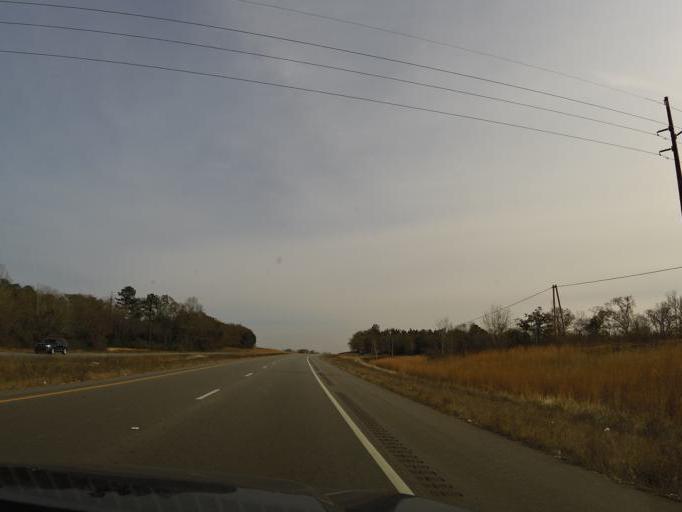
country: US
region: Alabama
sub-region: Houston County
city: Ashford
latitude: 31.1853
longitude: -85.2642
